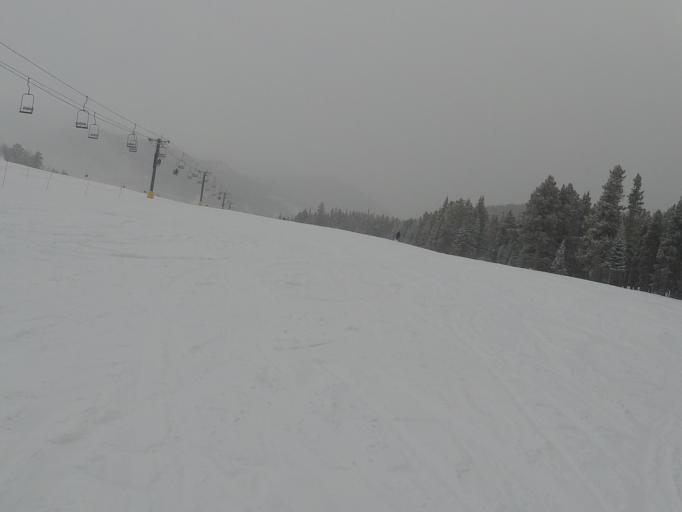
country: US
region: Montana
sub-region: Carbon County
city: Red Lodge
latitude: 45.1936
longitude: -109.3429
